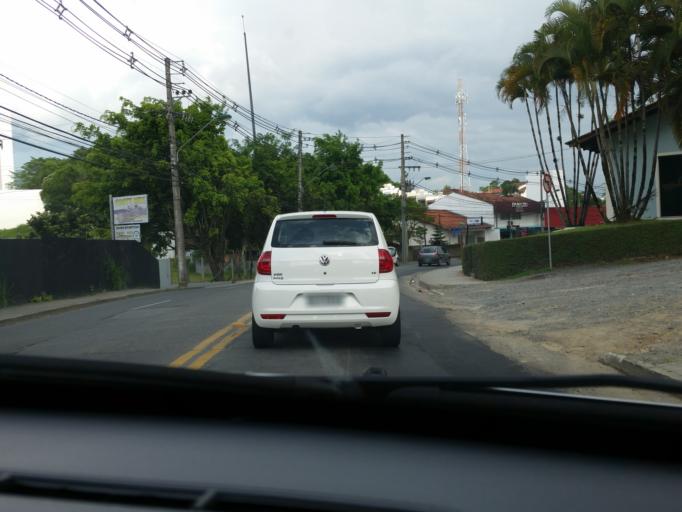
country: BR
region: Santa Catarina
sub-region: Blumenau
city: Blumenau
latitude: -26.9136
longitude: -49.1114
